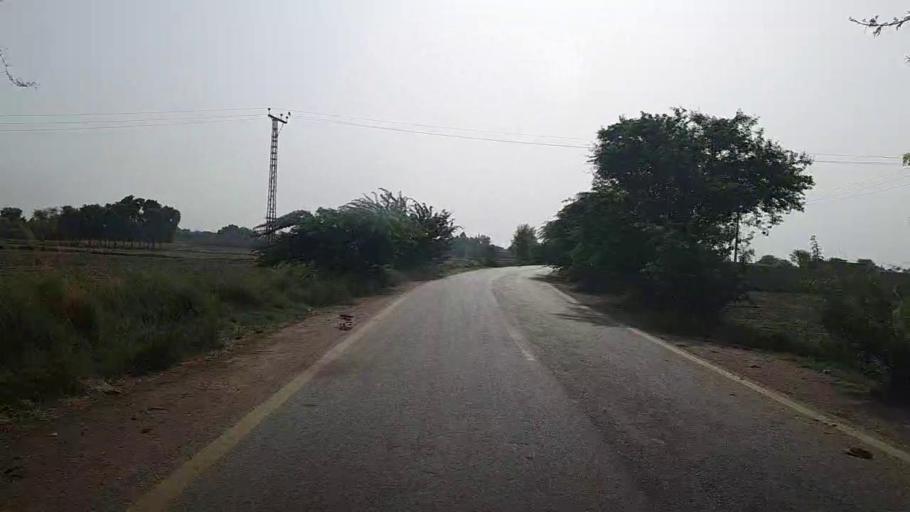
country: PK
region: Sindh
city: Khairpur Nathan Shah
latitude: 27.1083
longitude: 67.7618
